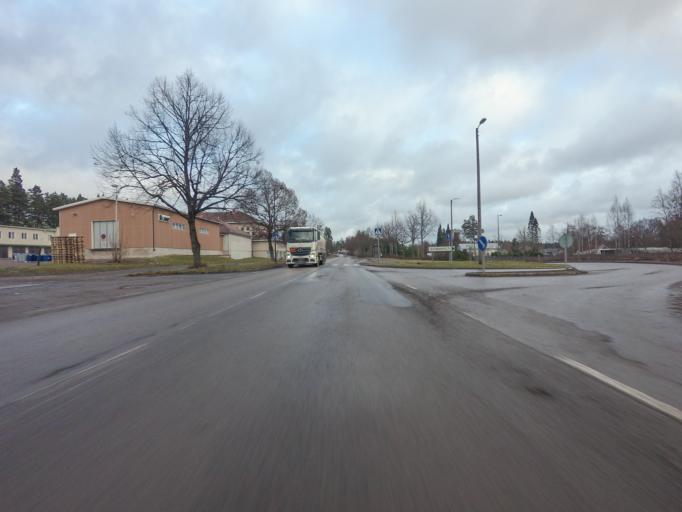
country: FI
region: Uusimaa
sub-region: Helsinki
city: Lohja
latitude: 60.2664
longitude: 24.1179
